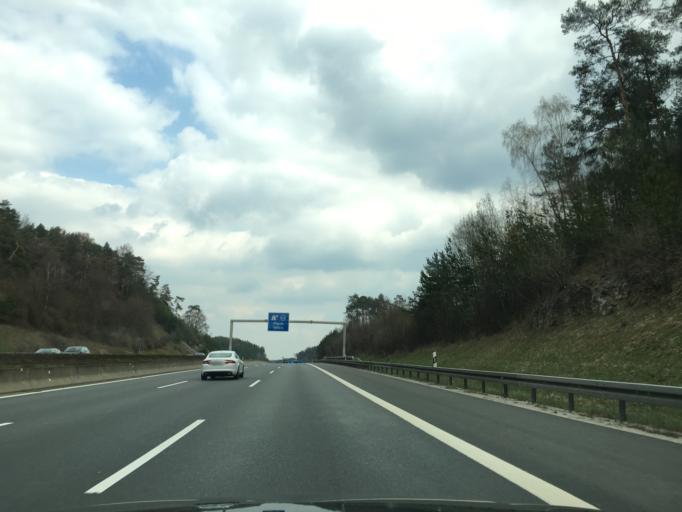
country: DE
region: Bavaria
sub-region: Regierungsbezirk Mittelfranken
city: Velden
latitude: 49.6558
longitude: 11.4579
